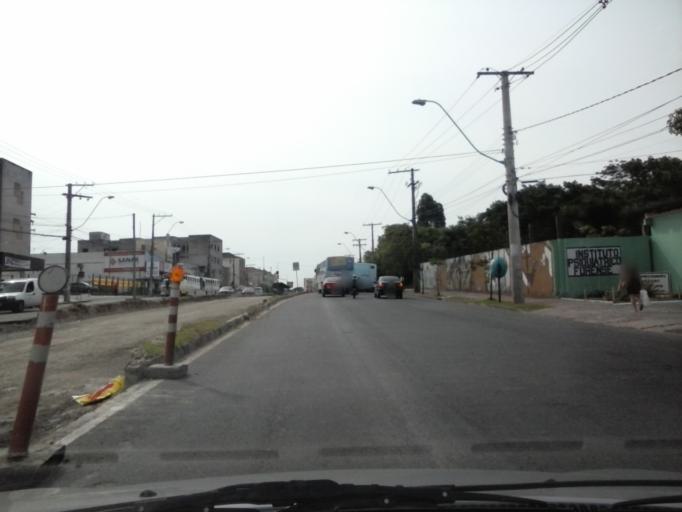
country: BR
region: Rio Grande do Sul
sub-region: Porto Alegre
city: Porto Alegre
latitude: -30.0627
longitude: -51.1868
